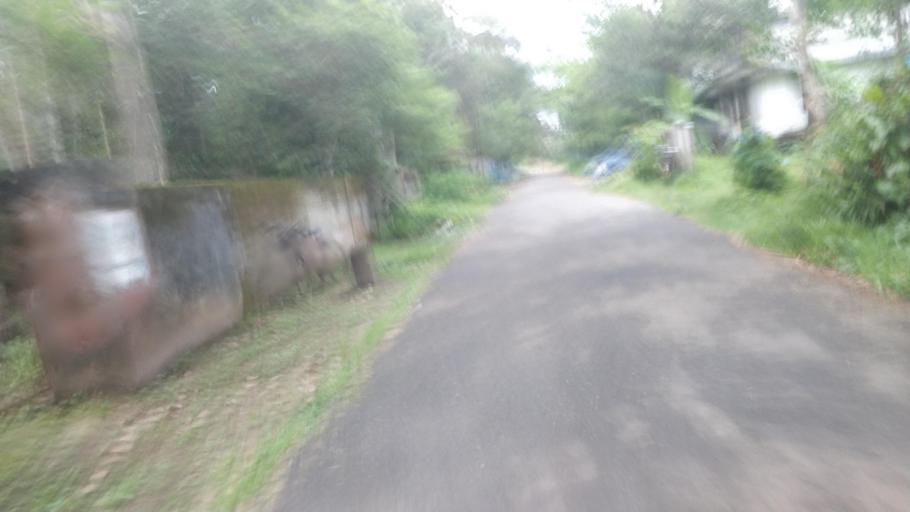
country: IN
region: Kerala
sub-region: Alappuzha
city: Vayalar
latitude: 9.7101
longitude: 76.3494
